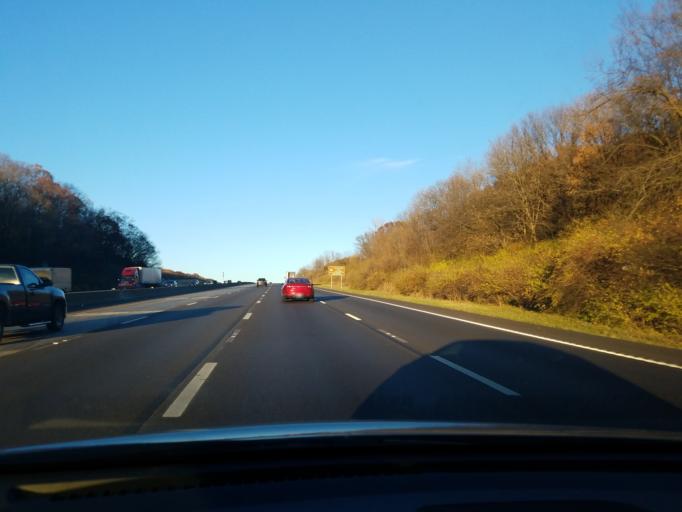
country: US
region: Missouri
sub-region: Jefferson County
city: High Ridge
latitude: 38.5110
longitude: -90.5537
